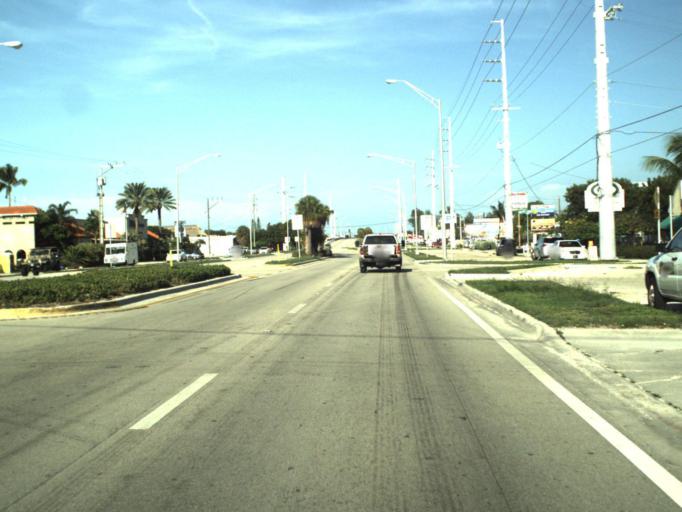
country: US
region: Florida
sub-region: Monroe County
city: Marathon
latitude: 24.7294
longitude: -81.0341
